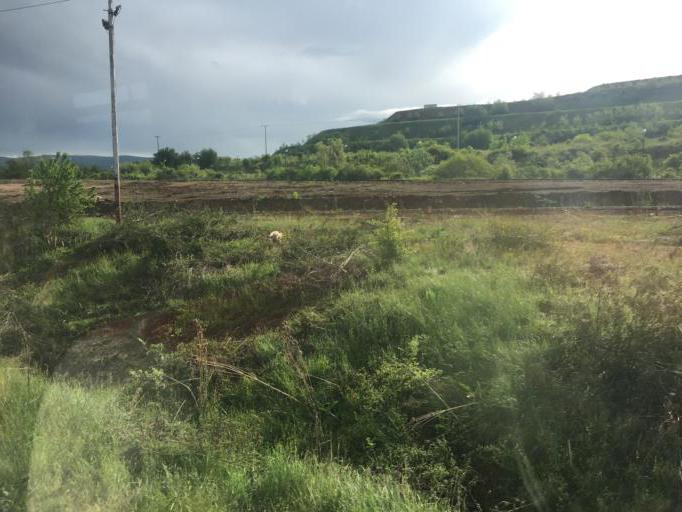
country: XK
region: Pristina
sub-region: Komuna e Drenasit
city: Glogovac
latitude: 42.6393
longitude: 20.9075
